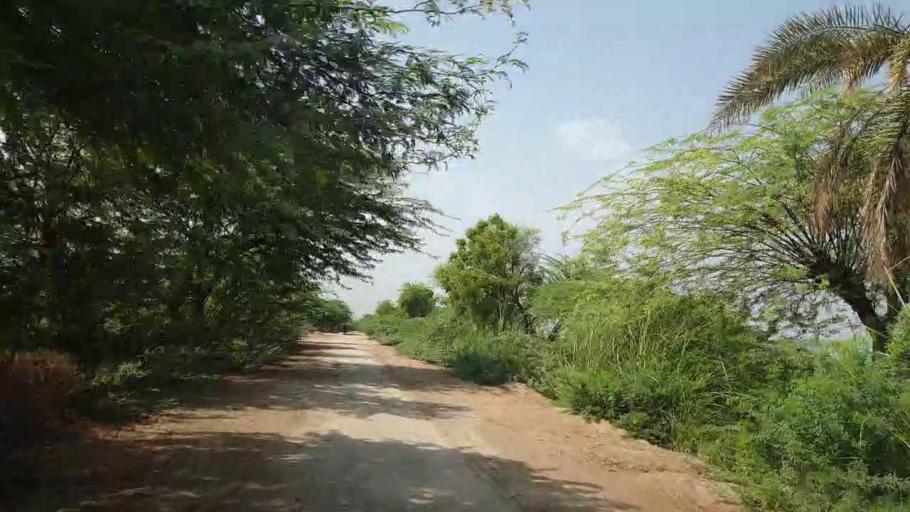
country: PK
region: Sindh
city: Lakhi
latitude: 27.8061
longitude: 68.7185
